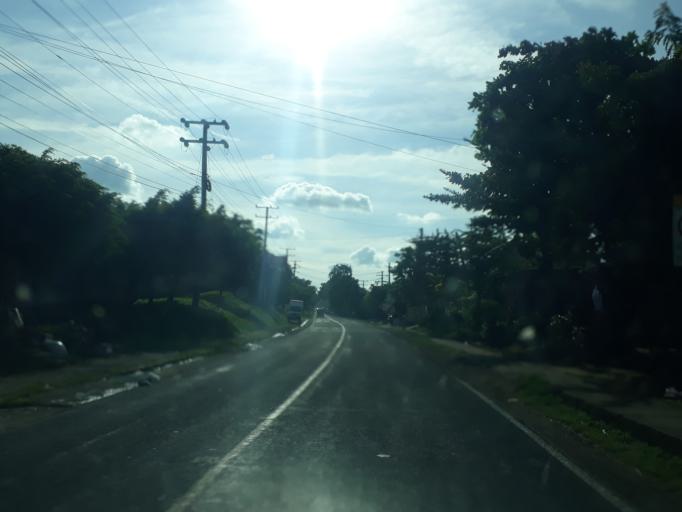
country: NI
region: Masaya
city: Masatepe
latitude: 11.9051
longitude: -86.1653
